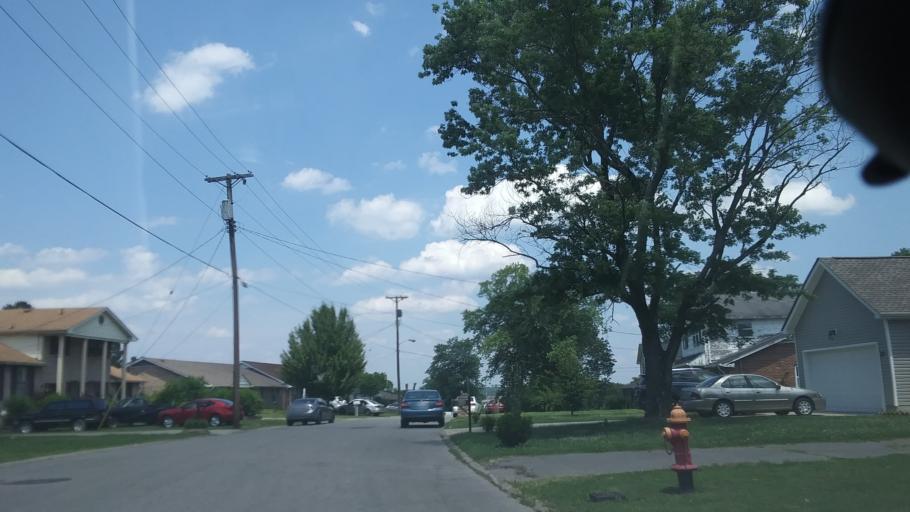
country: US
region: Tennessee
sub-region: Davidson County
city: Oak Hill
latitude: 36.0825
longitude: -86.7085
